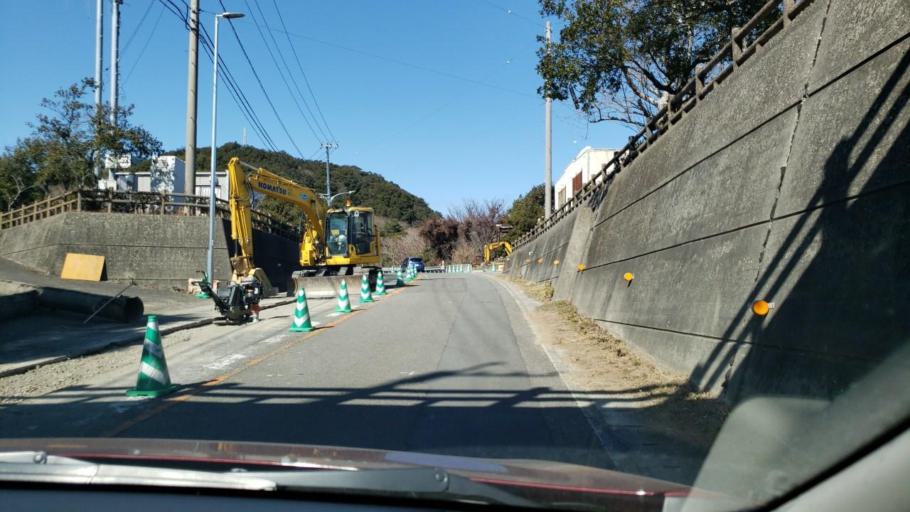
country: JP
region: Tokushima
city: Narutocho-mitsuishi
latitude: 34.2378
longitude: 134.6126
